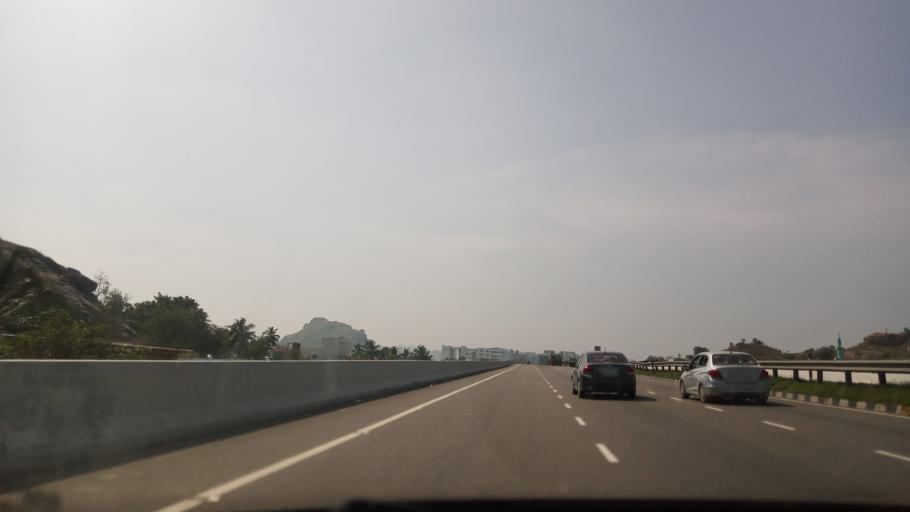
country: IN
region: Tamil Nadu
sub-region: Vellore
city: Arcot
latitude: 12.9384
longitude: 79.2461
